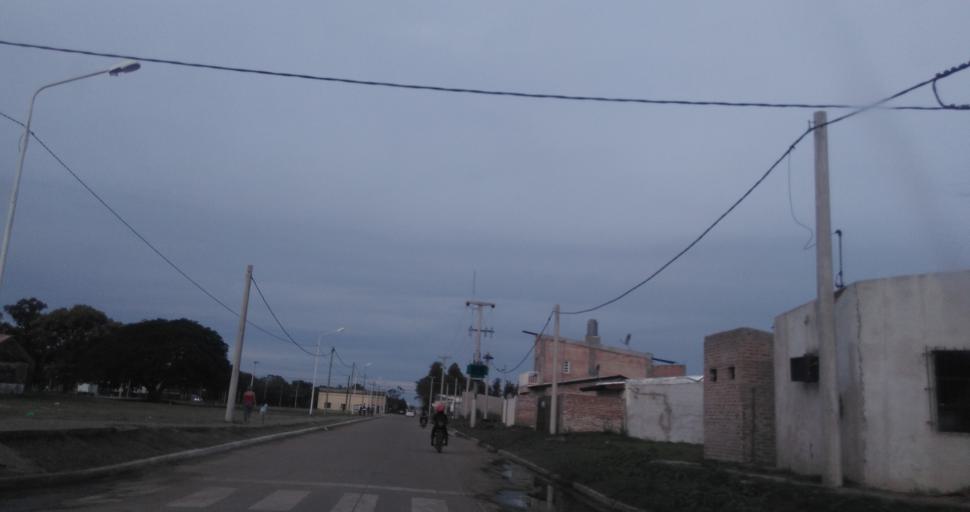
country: AR
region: Chaco
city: Fontana
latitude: -27.4183
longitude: -59.0349
